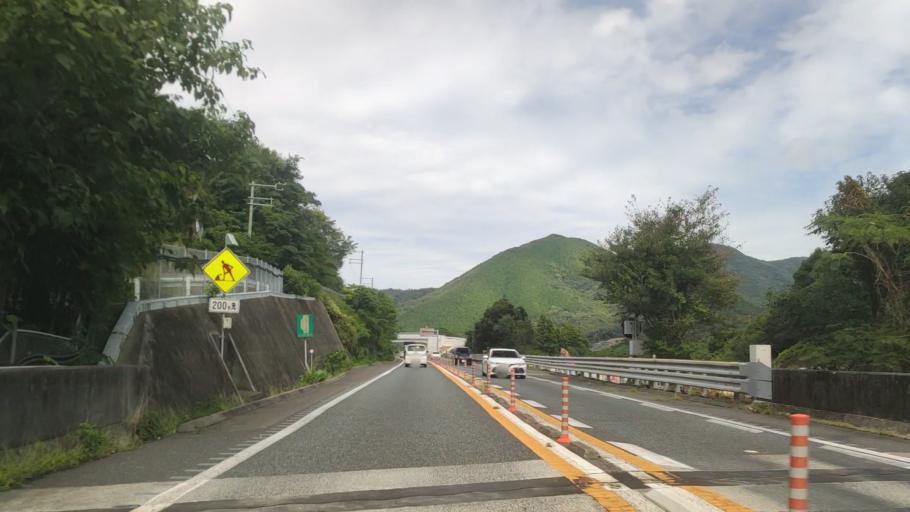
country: JP
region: Wakayama
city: Gobo
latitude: 33.9888
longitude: 135.1990
